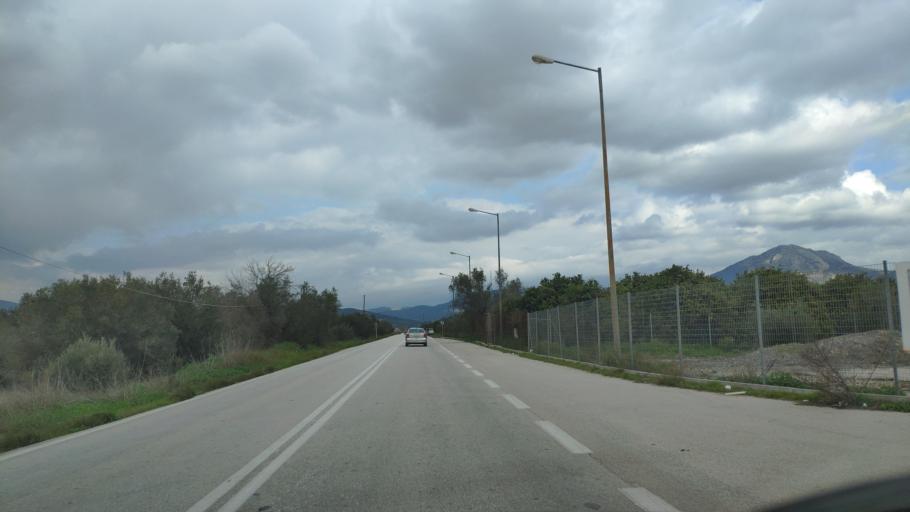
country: GR
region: Peloponnese
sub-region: Nomos Argolidos
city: Koutsopodi
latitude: 37.6969
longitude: 22.7221
